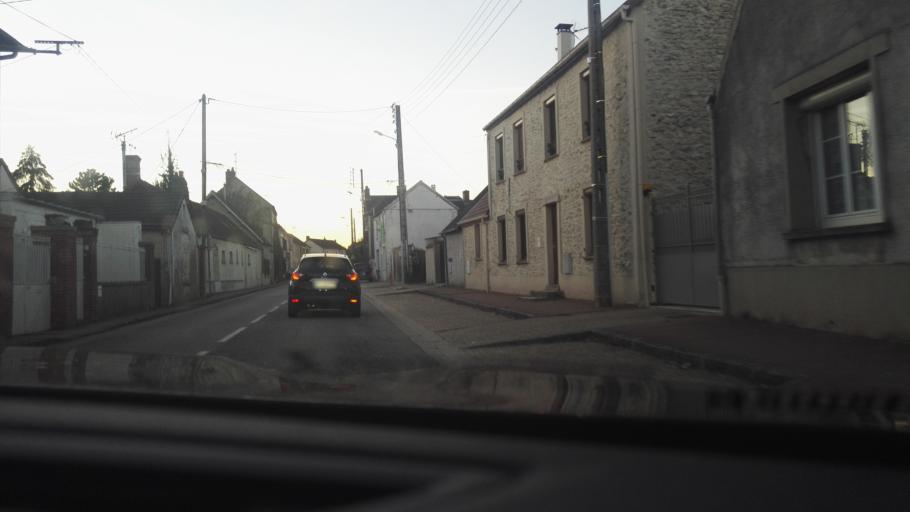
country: FR
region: Ile-de-France
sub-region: Departement des Yvelines
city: Longnes
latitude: 48.9195
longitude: 1.5867
